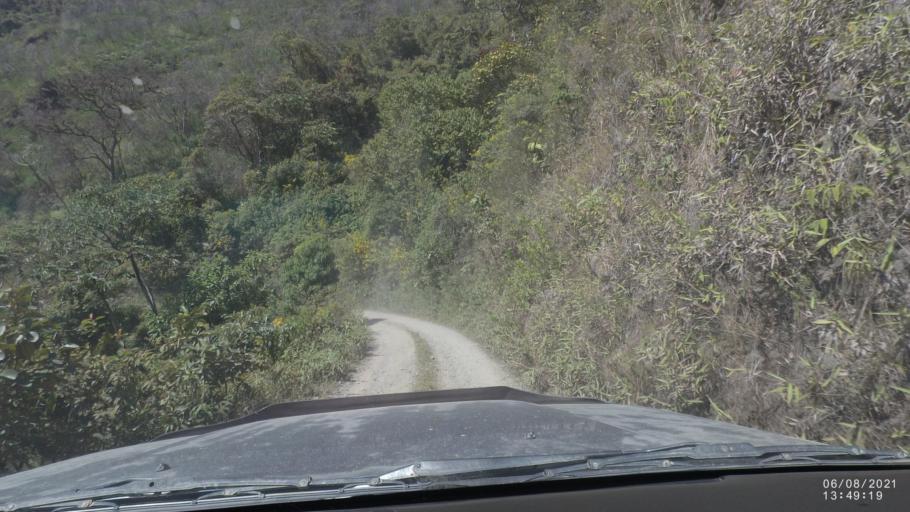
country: BO
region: La Paz
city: Quime
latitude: -16.6613
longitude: -66.7223
